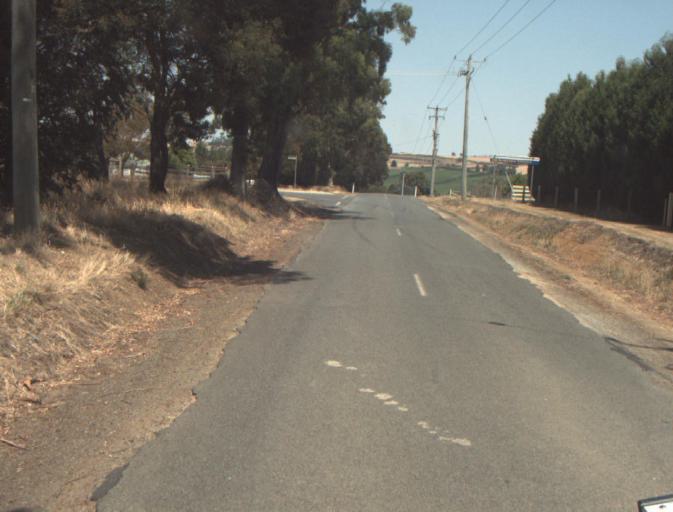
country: AU
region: Tasmania
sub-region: Launceston
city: Newstead
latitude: -41.4999
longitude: 147.2065
